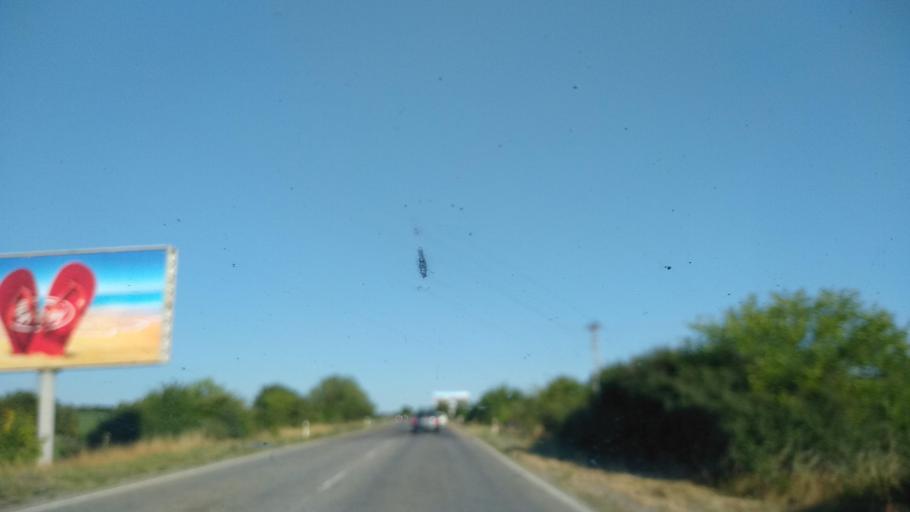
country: BG
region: Gabrovo
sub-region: Obshtina Dryanovo
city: Dryanovo
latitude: 43.0868
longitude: 25.4373
